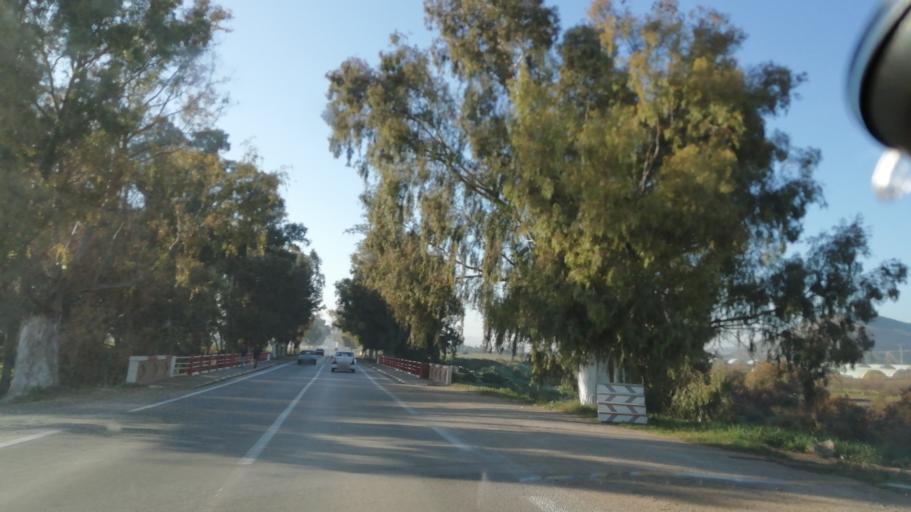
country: DZ
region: Tlemcen
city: Remchi
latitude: 35.0534
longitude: -1.5018
